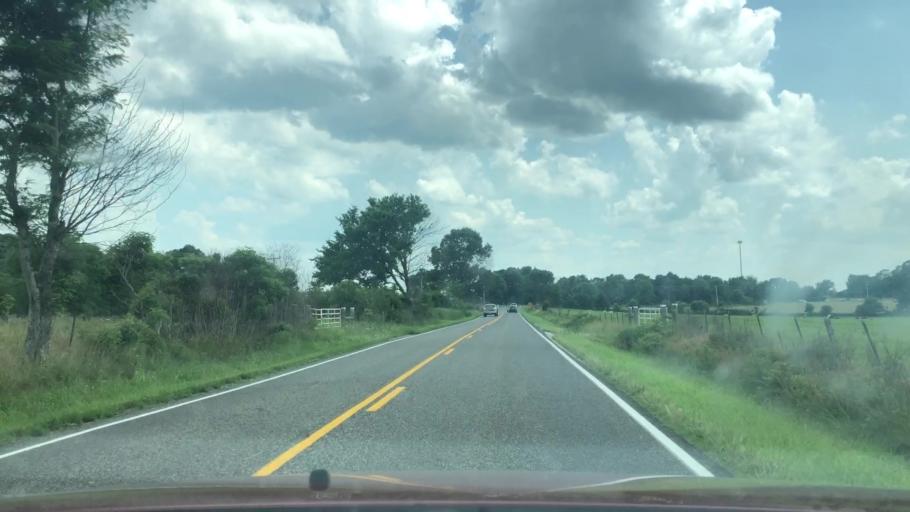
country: US
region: Missouri
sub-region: Christian County
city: Ozark
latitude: 36.9388
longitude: -93.2536
